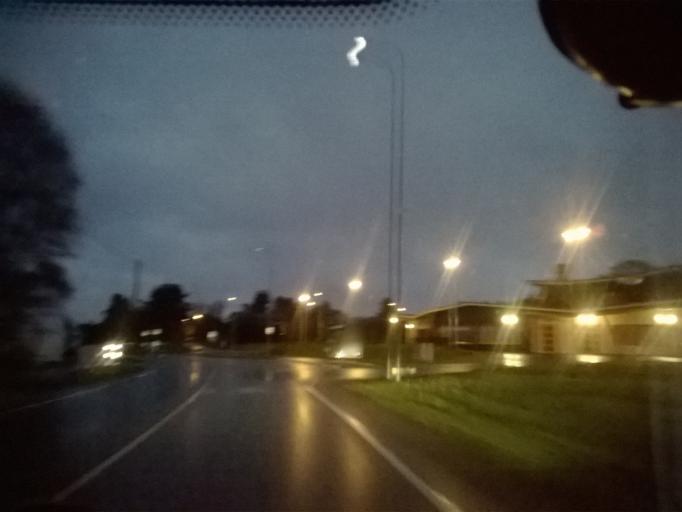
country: EE
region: Harju
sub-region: Viimsi vald
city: Viimsi
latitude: 59.5143
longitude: 24.8494
